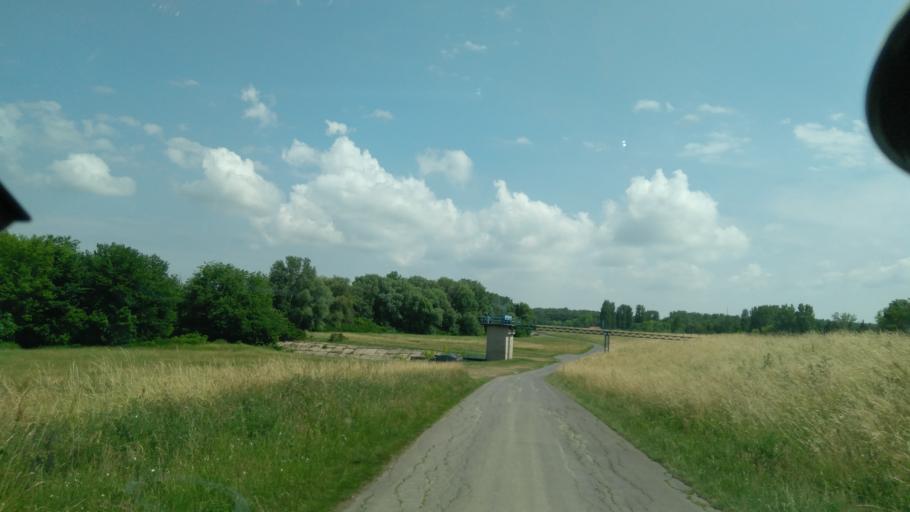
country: HU
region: Bekes
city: Bekes
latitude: 46.7636
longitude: 21.1504
